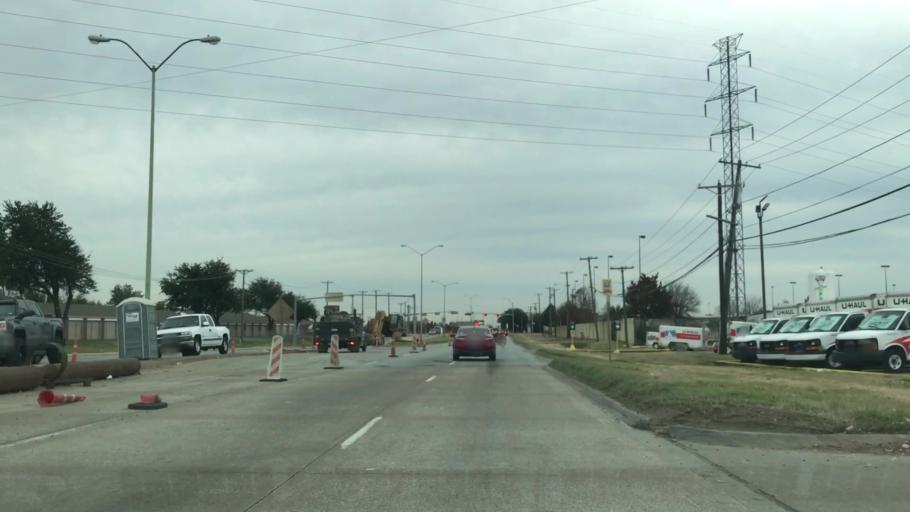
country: US
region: Texas
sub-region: Dallas County
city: Farmers Branch
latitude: 32.8573
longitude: -96.8806
